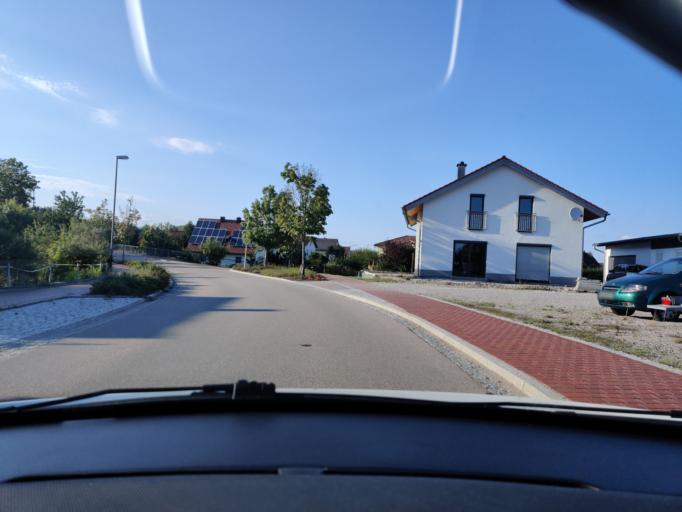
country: DE
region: Bavaria
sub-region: Upper Palatinate
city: Schwarzenfeld
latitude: 49.3946
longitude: 12.1360
